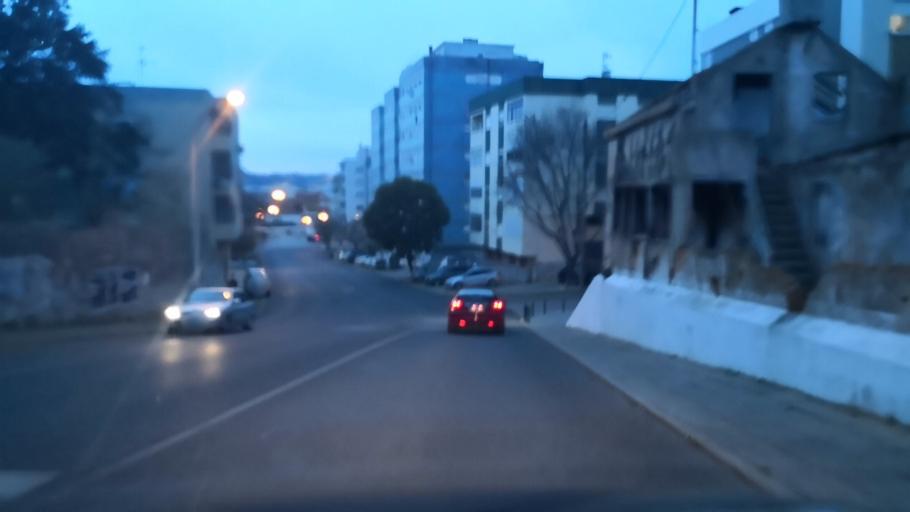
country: PT
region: Setubal
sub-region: Setubal
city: Setubal
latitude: 38.5227
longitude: -8.8725
